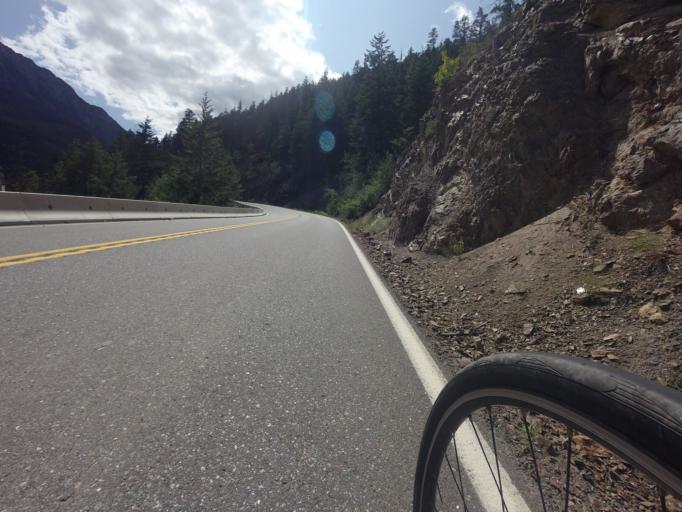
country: CA
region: British Columbia
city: Lillooet
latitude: 50.6555
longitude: -122.0006
